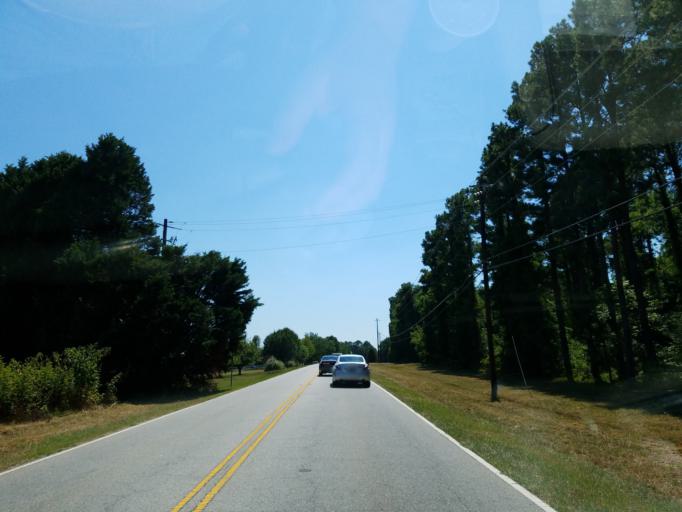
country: US
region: Georgia
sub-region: Clayton County
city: Lovejoy
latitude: 33.4567
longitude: -84.2997
